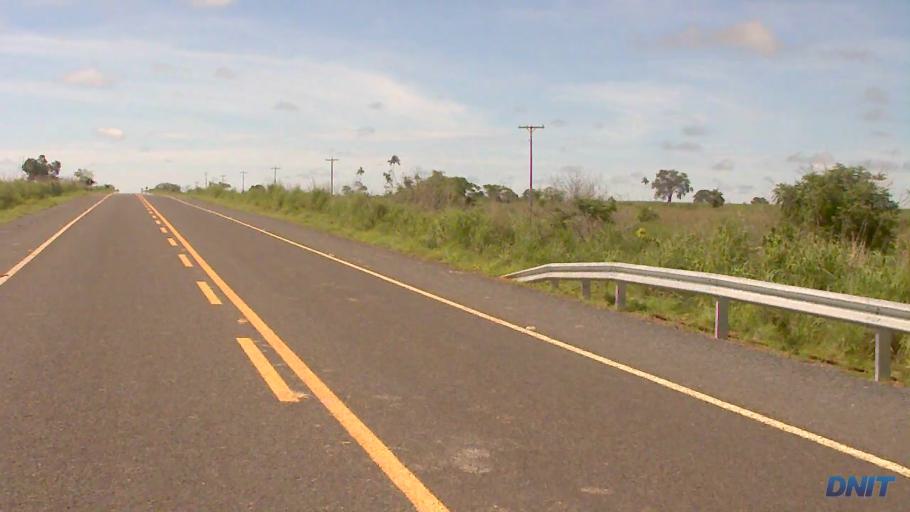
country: BR
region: Goias
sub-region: Sao Miguel Do Araguaia
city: Sao Miguel do Araguaia
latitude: -13.3480
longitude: -50.1502
